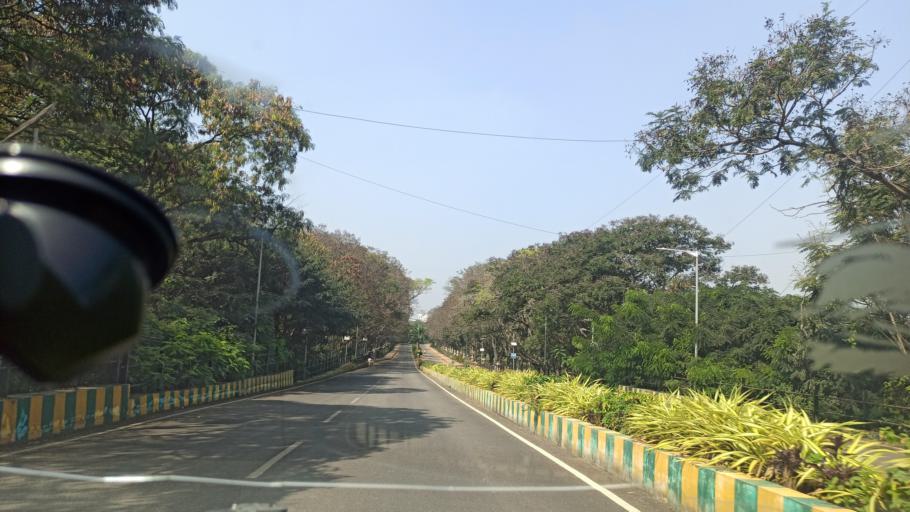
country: IN
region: Karnataka
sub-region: Bangalore Urban
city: Yelahanka
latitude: 13.0740
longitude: 77.5888
